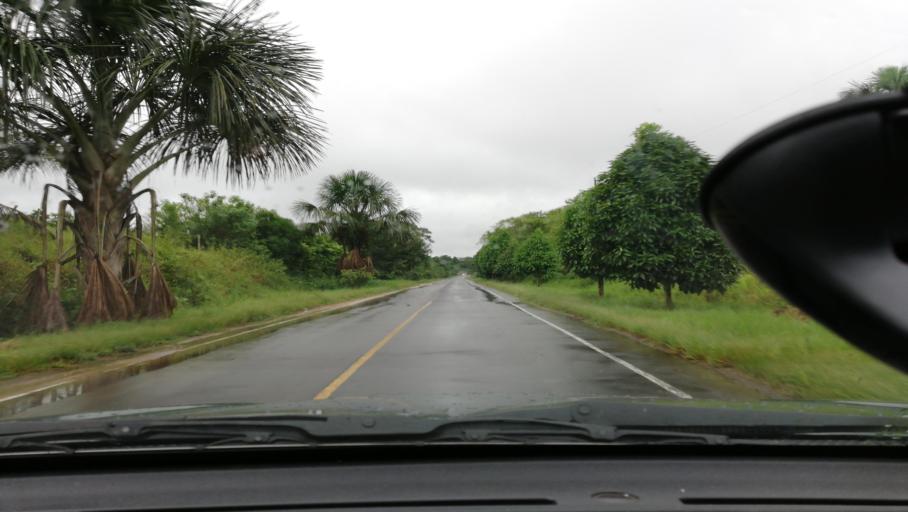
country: PE
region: Loreto
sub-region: Provincia de Maynas
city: San Juan
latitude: -4.1409
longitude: -73.4707
